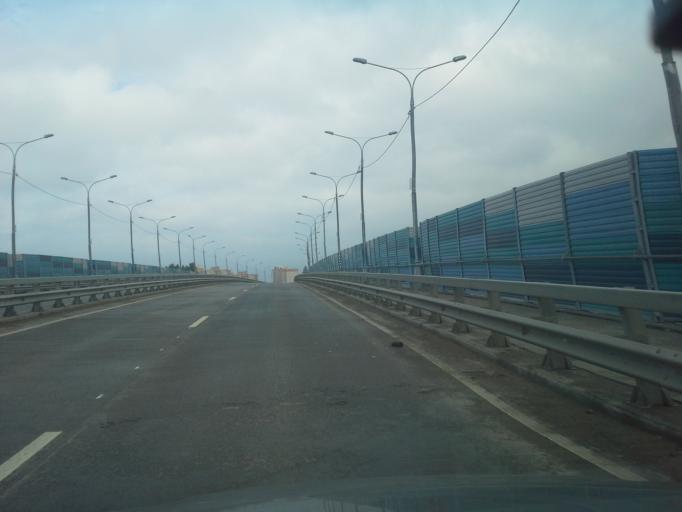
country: RU
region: Moskovskaya
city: Tuchkovo
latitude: 55.5969
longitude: 36.4819
